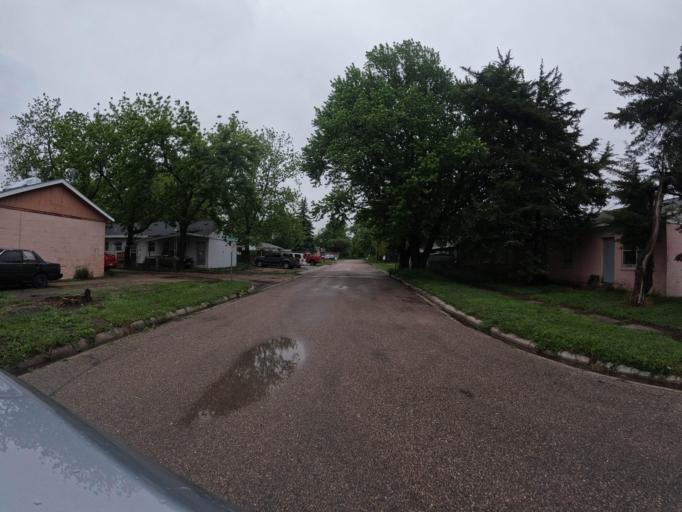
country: US
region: Nebraska
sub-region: Clay County
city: Harvard
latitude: 40.6264
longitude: -98.0929
